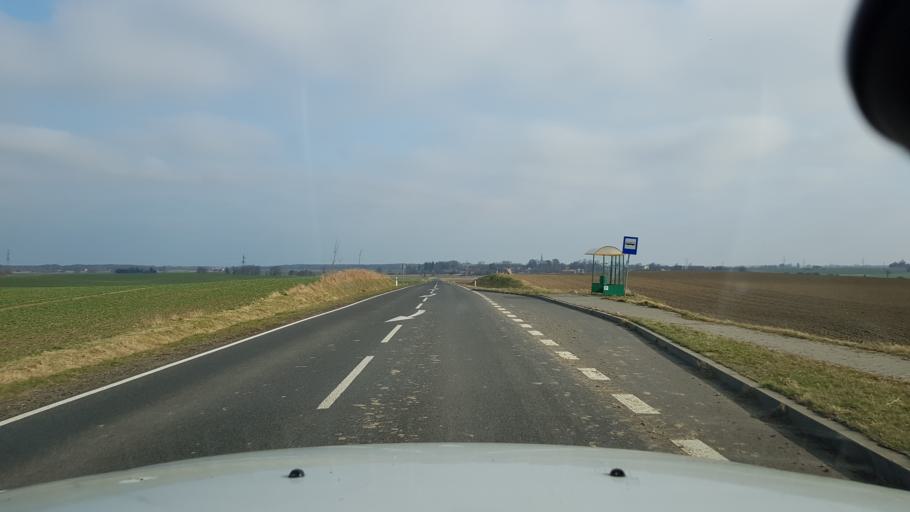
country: PL
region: West Pomeranian Voivodeship
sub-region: Powiat koszalinski
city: Sianow
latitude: 54.2816
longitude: 16.2705
